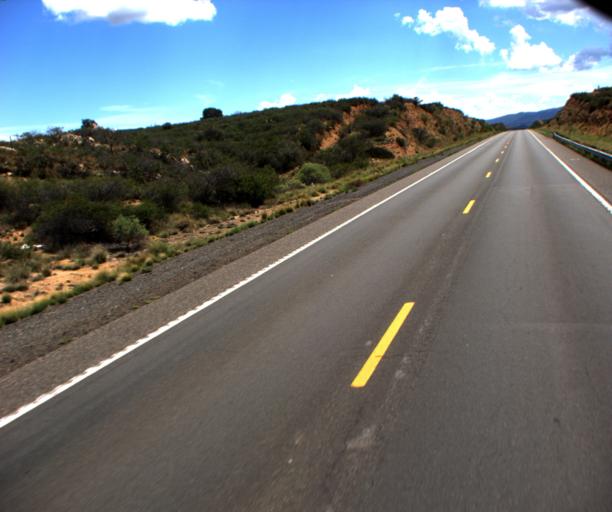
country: US
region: Arizona
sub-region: Yavapai County
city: Dewey-Humboldt
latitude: 34.5288
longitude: -112.1036
